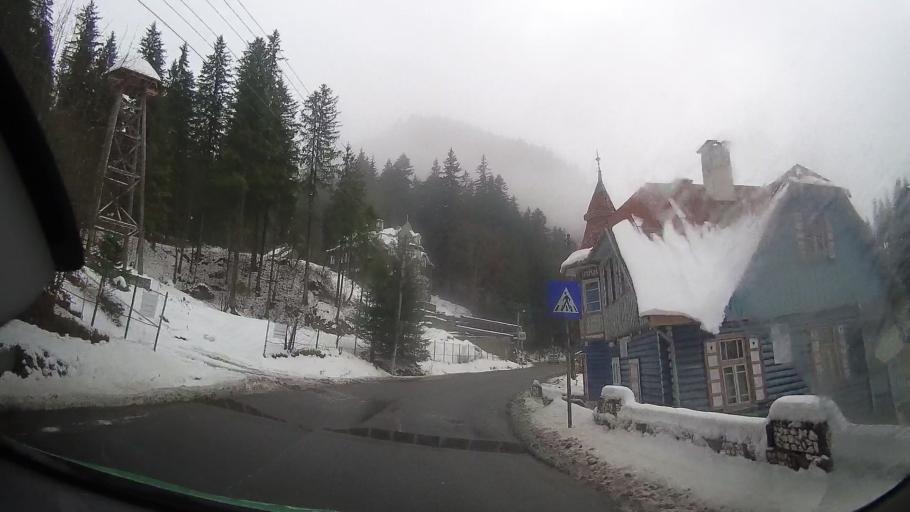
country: RO
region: Neamt
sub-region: Comuna Bicaz Chei
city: Bicaz Chei
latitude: 46.7955
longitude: 25.8013
